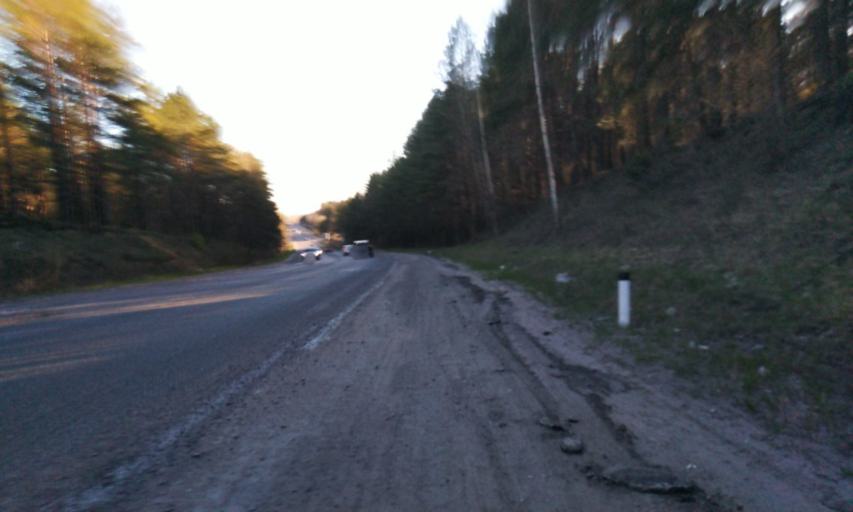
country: RU
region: Leningrad
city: Toksovo
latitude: 60.1316
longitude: 30.5230
